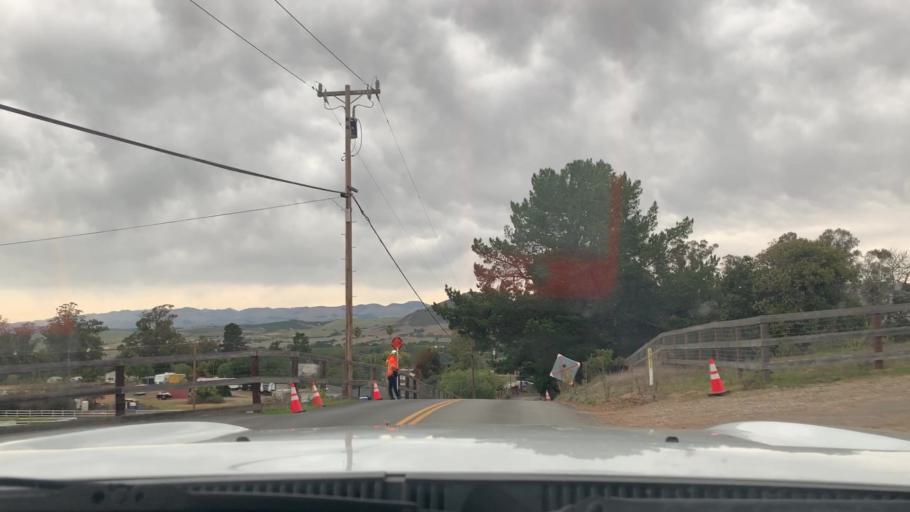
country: US
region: California
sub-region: San Luis Obispo County
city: Callender
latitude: 35.0729
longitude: -120.5525
